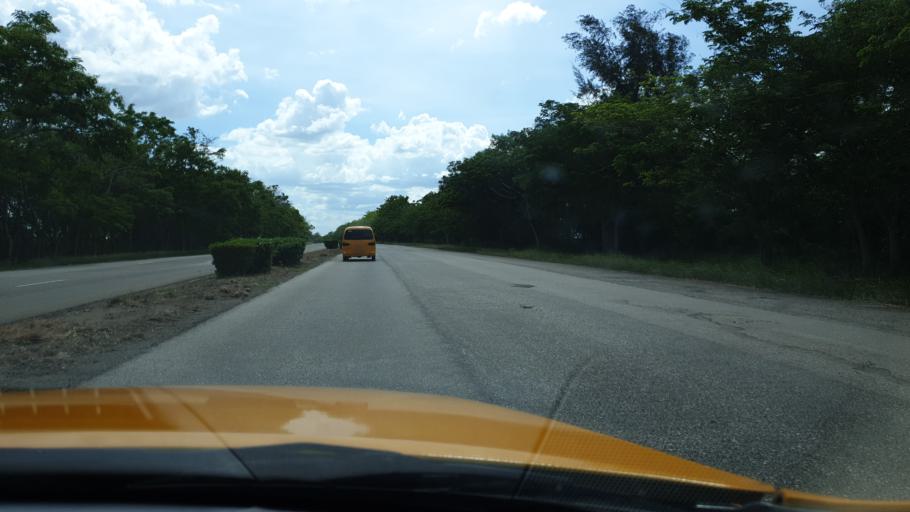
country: CU
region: Cienfuegos
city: Cruces
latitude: 22.4551
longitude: -80.3059
